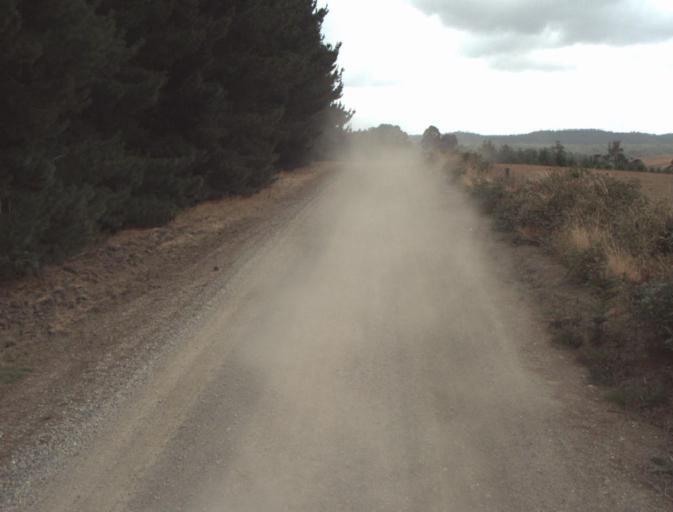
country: AU
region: Tasmania
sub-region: Launceston
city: Mayfield
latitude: -41.1661
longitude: 147.2121
